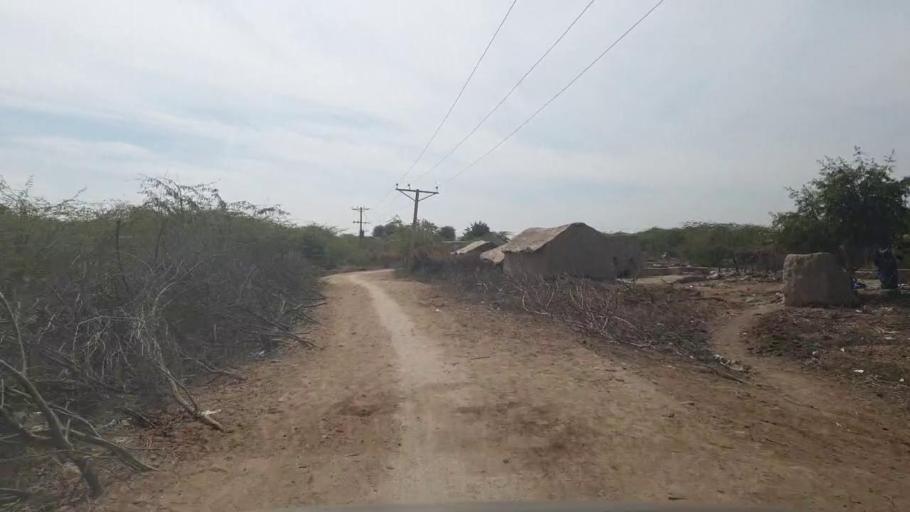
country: PK
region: Sindh
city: Kunri
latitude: 25.3090
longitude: 69.5762
